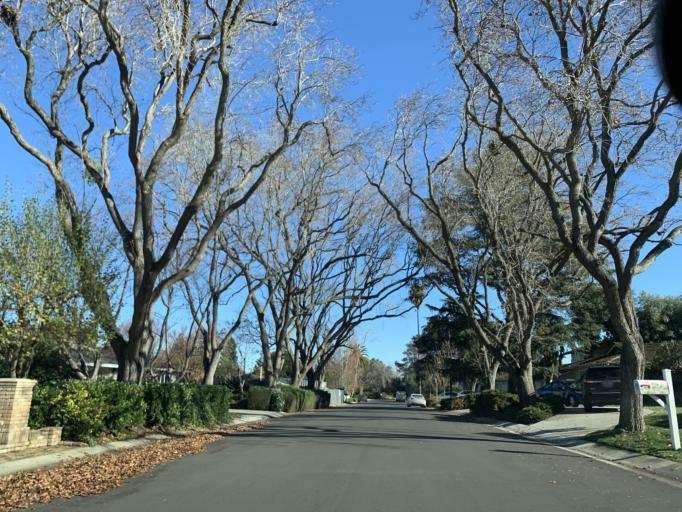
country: US
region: California
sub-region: Santa Clara County
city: Los Altos
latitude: 37.3801
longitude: -122.1041
